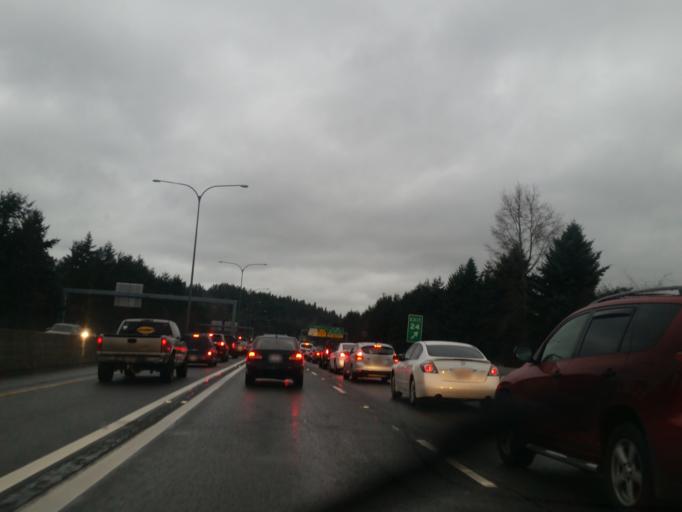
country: US
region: Washington
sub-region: King County
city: Bothell
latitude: 47.7621
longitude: -122.1849
